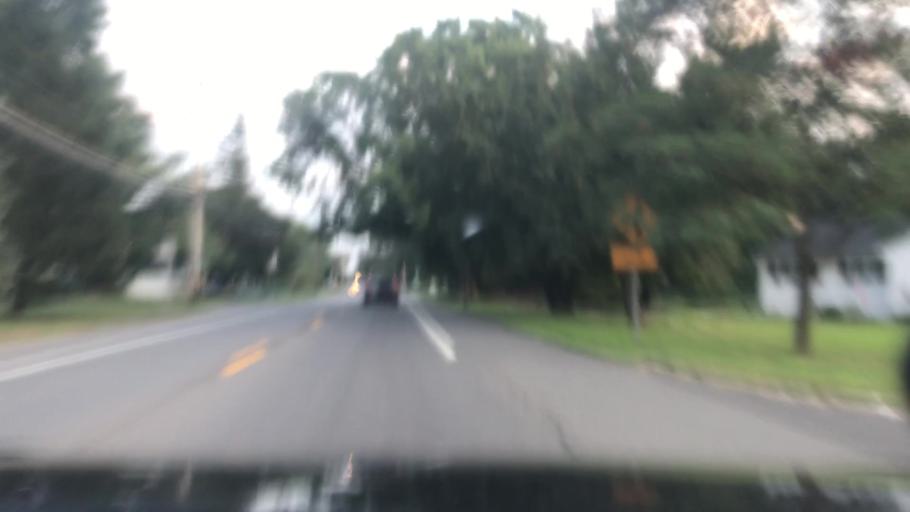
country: US
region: New Jersey
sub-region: Ocean County
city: Silver Ridge
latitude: 39.9790
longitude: -74.2087
